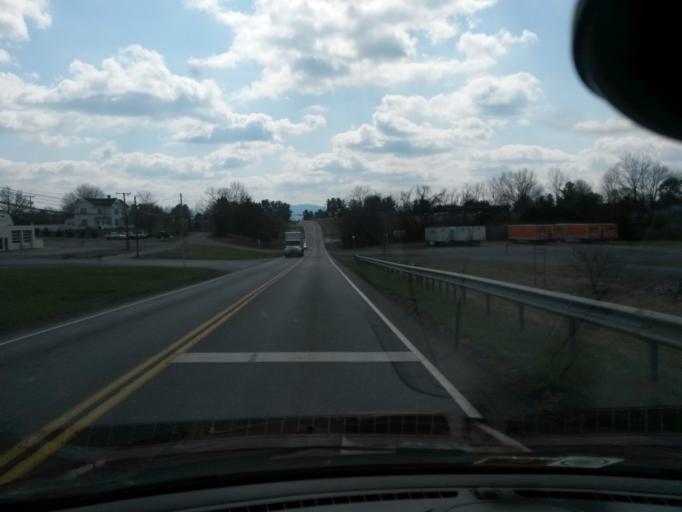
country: US
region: Virginia
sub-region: Augusta County
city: Weyers Cave
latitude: 38.2877
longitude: -78.9184
